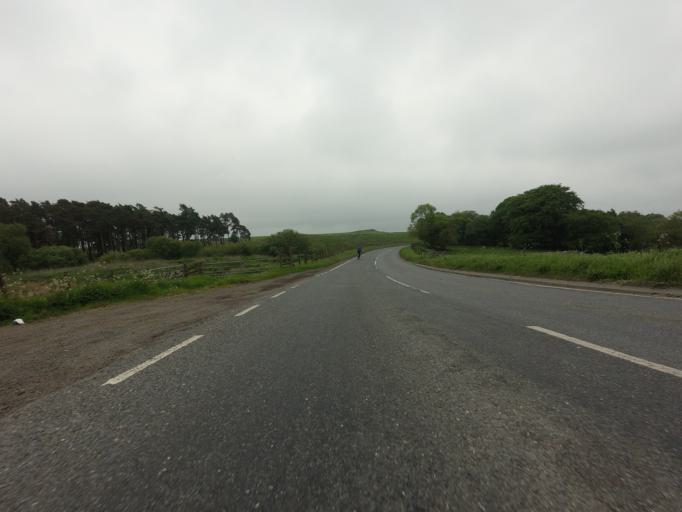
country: GB
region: Scotland
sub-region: Fife
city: Townhill
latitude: 56.1168
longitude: -3.4445
